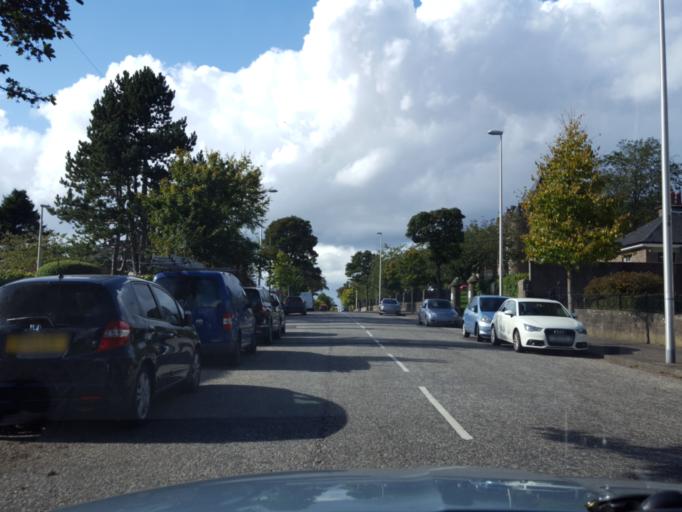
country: GB
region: Scotland
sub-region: Dundee City
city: Dundee
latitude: 56.4606
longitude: -3.0067
